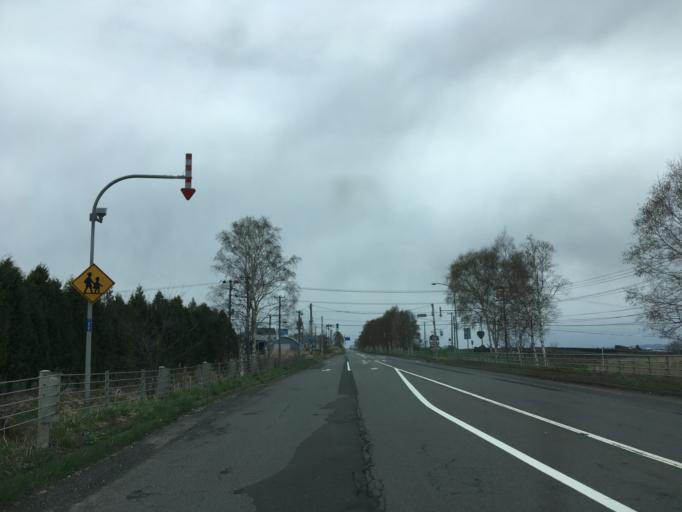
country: JP
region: Hokkaido
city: Chitose
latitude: 42.9146
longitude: 141.8104
